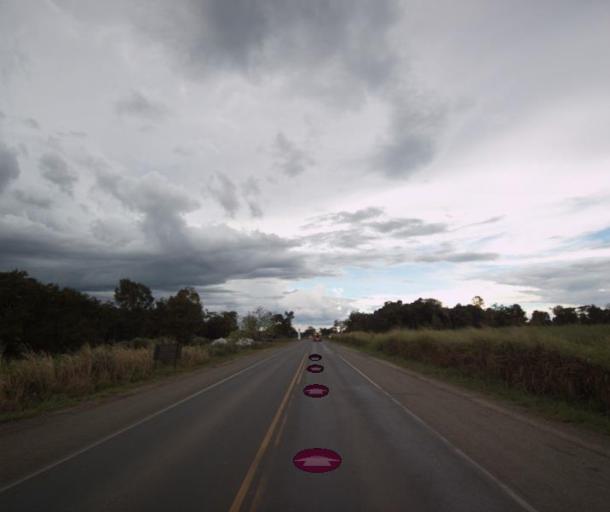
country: BR
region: Goias
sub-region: Itapaci
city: Itapaci
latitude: -15.0261
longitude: -49.4288
